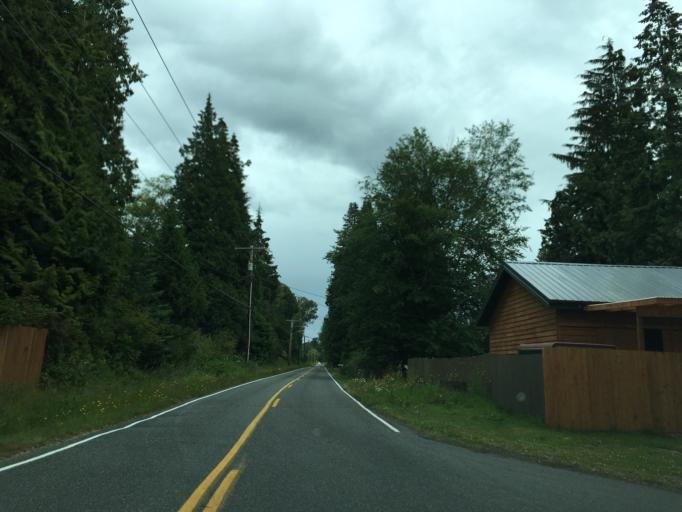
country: US
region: Washington
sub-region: Whatcom County
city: Birch Bay
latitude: 48.9433
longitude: -122.7557
